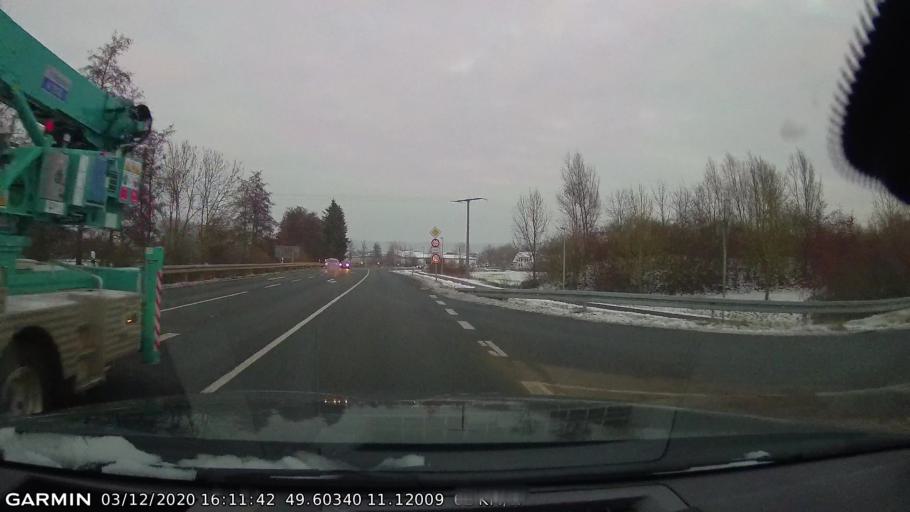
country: DE
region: Bavaria
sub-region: Upper Franconia
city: Dormitz
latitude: 49.6036
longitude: 11.1202
